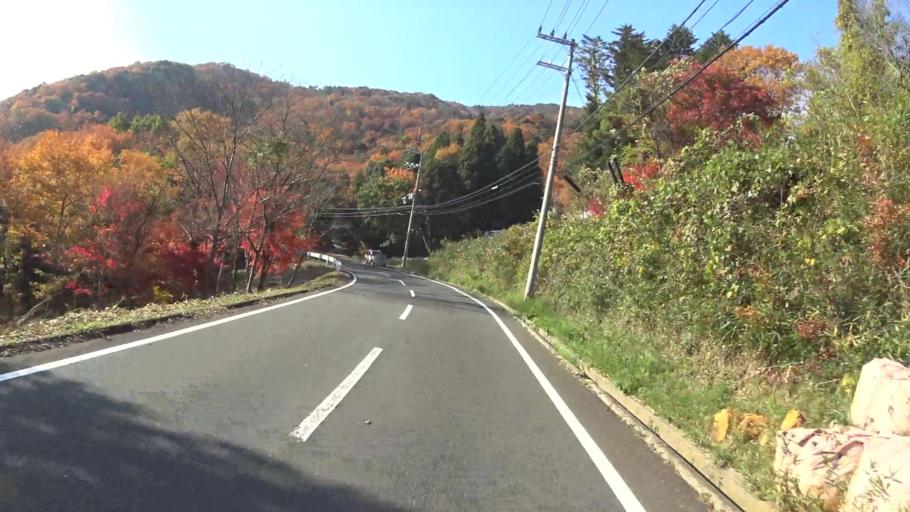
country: JP
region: Kyoto
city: Maizuru
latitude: 35.5332
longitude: 135.3950
